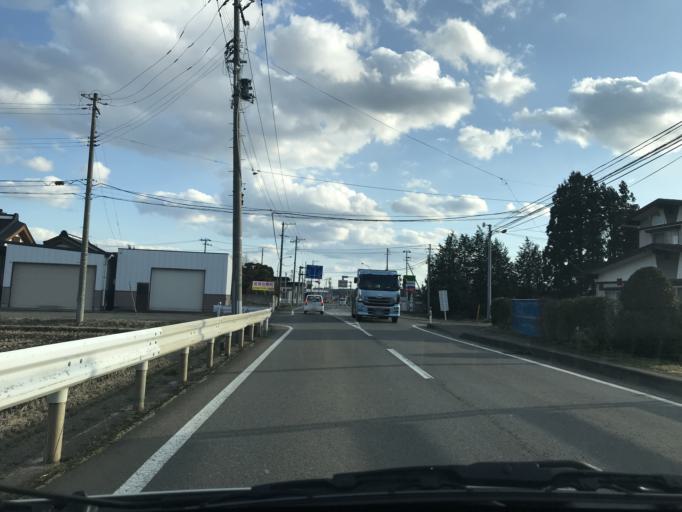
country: JP
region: Iwate
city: Kitakami
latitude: 39.3058
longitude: 141.0339
